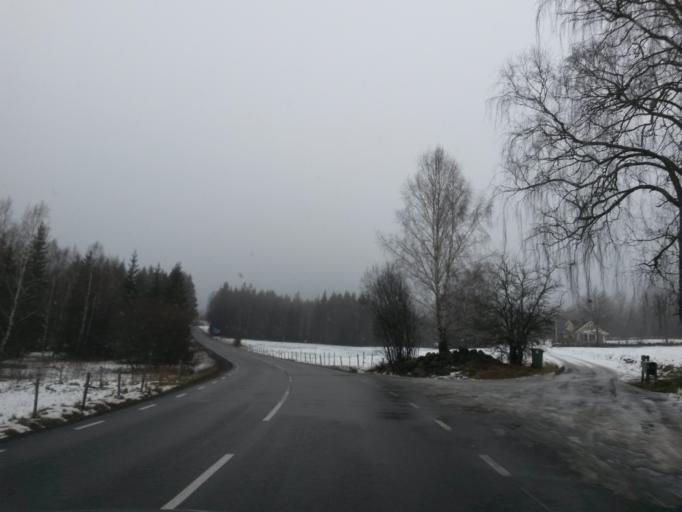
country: SE
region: Vaestra Goetaland
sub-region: Ulricehamns Kommun
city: Ulricehamn
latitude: 57.6704
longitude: 13.4020
